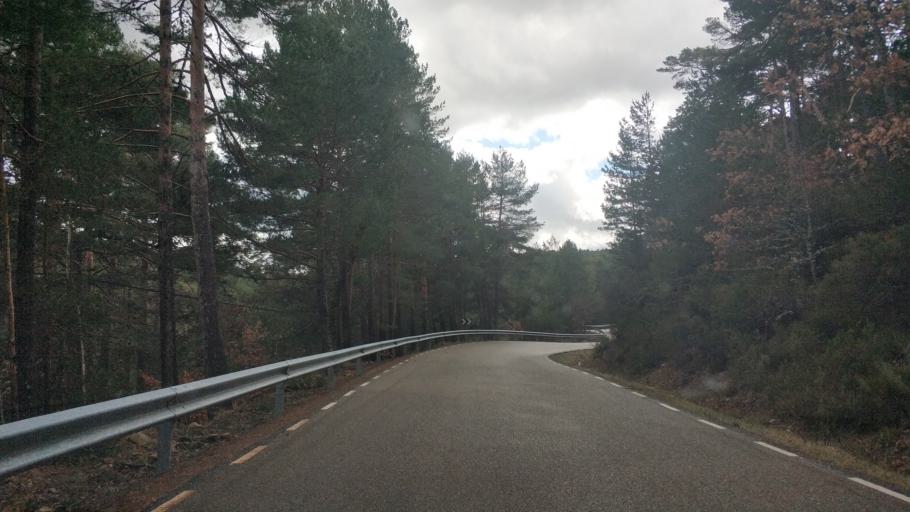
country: ES
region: Castille and Leon
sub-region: Provincia de Burgos
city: Quintanar de la Sierra
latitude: 42.0121
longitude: -3.0196
